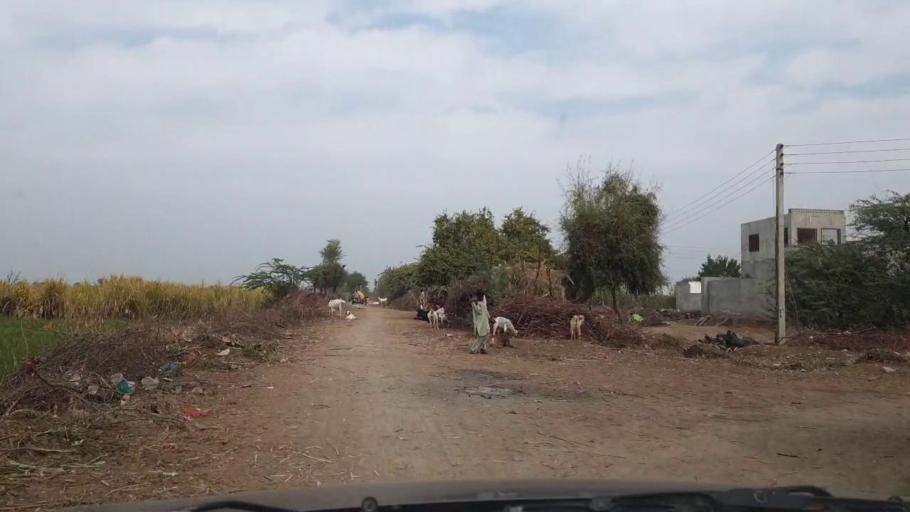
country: PK
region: Sindh
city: Sinjhoro
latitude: 26.0723
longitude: 68.8285
